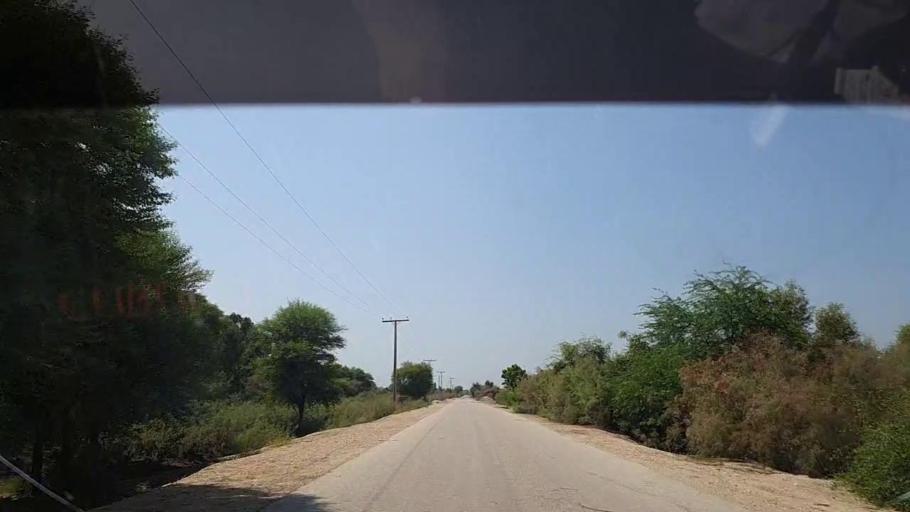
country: PK
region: Sindh
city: Ghauspur
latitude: 28.1565
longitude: 69.1527
